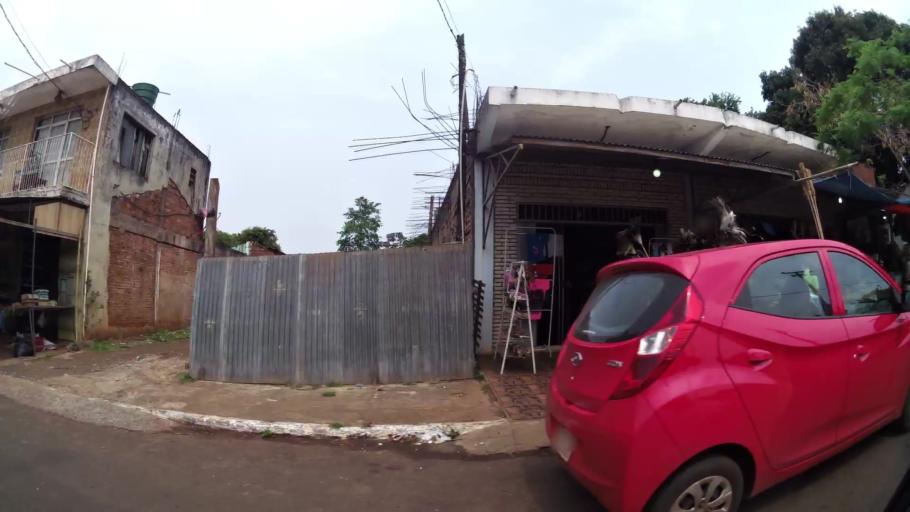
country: BR
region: Parana
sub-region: Foz Do Iguacu
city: Foz do Iguacu
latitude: -25.5589
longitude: -54.6046
